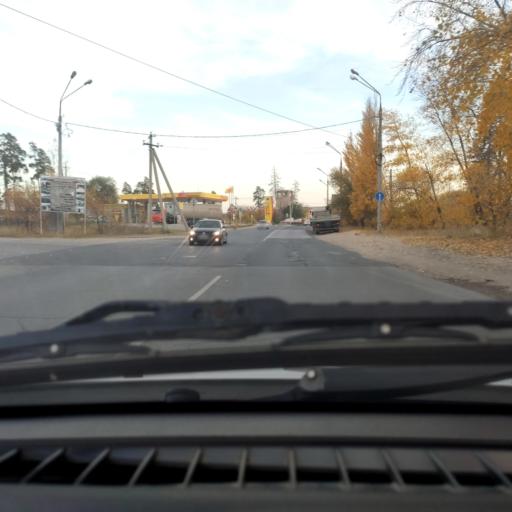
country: RU
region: Samara
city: Zhigulevsk
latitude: 53.4685
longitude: 49.5474
